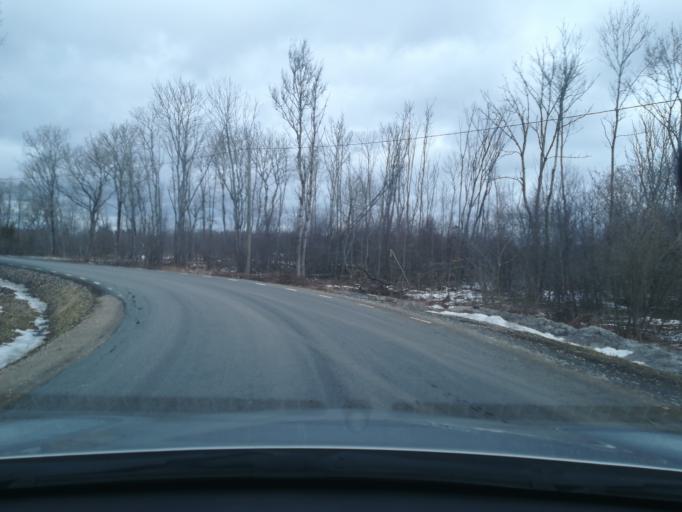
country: EE
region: Harju
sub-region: Saue linn
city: Saue
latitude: 59.3546
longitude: 24.5388
